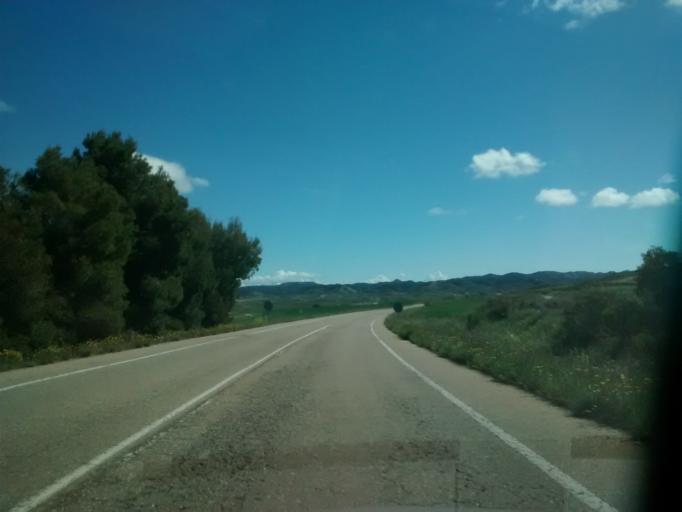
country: ES
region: Aragon
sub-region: Provincia de Zaragoza
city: Lecinena
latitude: 41.8046
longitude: -0.5981
